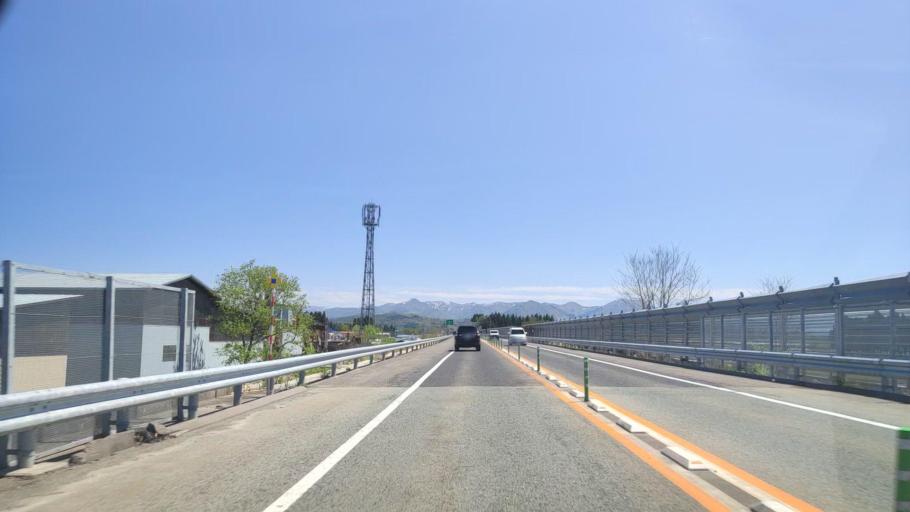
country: JP
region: Yamagata
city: Obanazawa
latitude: 38.6252
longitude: 140.3777
